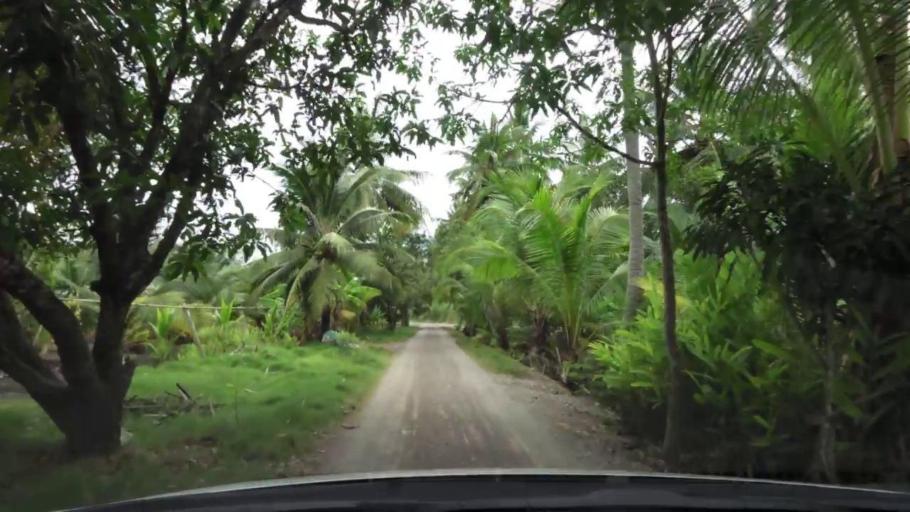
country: TH
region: Ratchaburi
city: Damnoen Saduak
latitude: 13.5528
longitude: 99.9924
